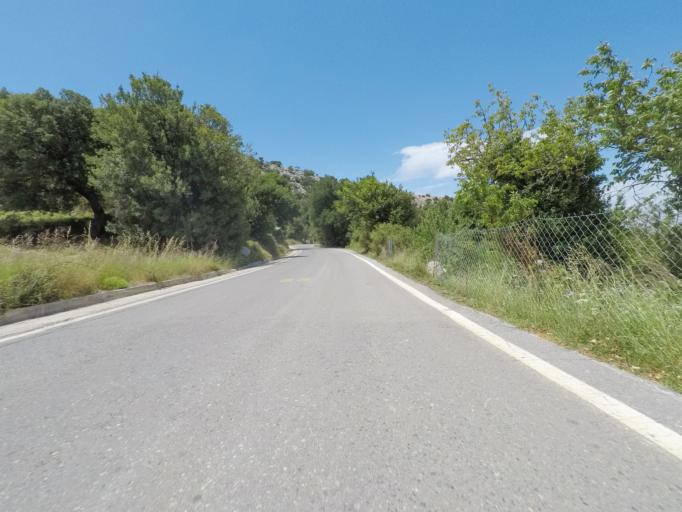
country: GR
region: Crete
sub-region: Nomos Irakleiou
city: Mokhos
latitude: 35.1725
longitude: 25.4370
